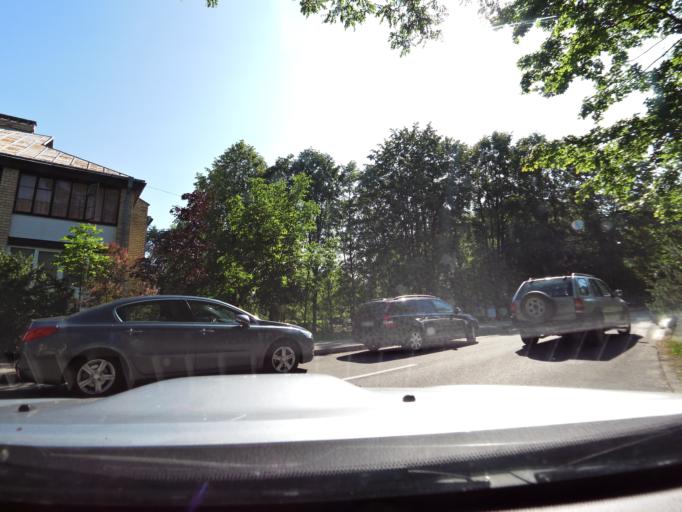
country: LT
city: Birstonas
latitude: 54.6055
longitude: 24.0249
